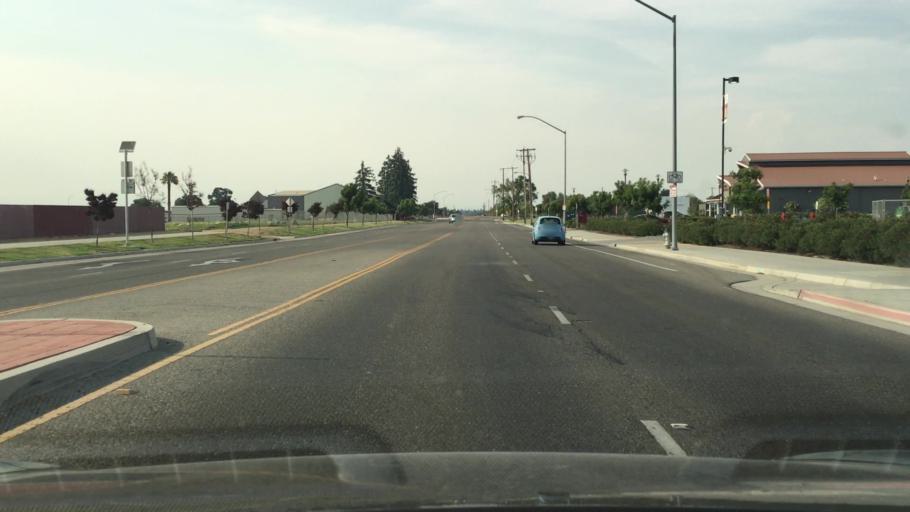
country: US
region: California
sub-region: Fresno County
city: Clovis
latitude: 36.8126
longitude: -119.7362
